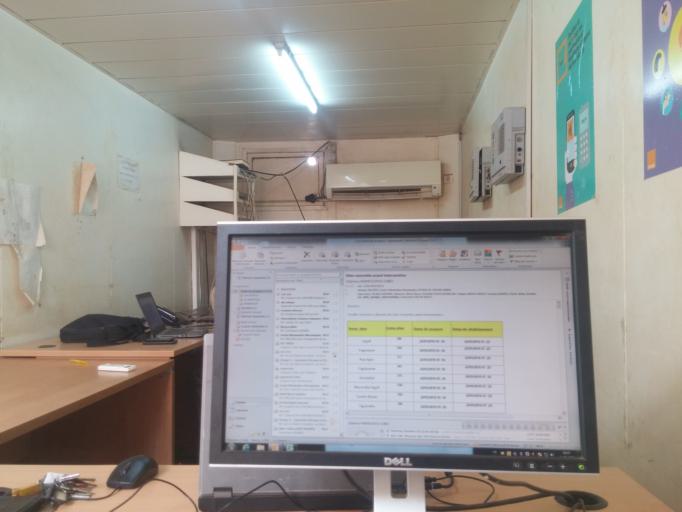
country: NE
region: Niamey
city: Niamey
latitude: 13.4908
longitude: 2.1422
